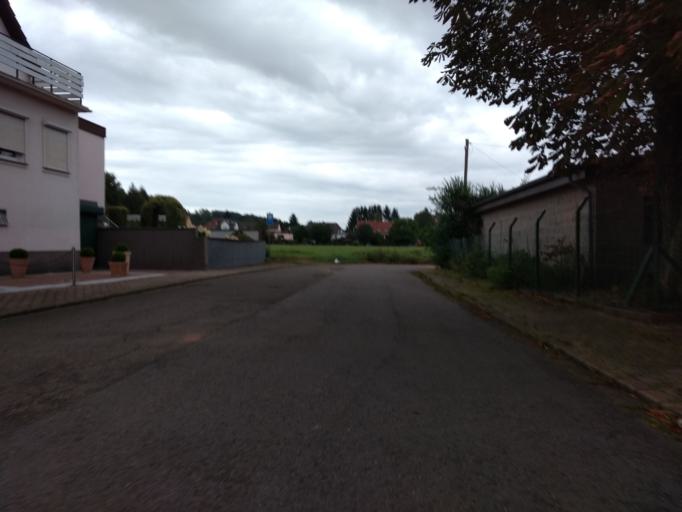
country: DE
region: Saarland
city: Nalbach
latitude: 49.3694
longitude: 6.7650
